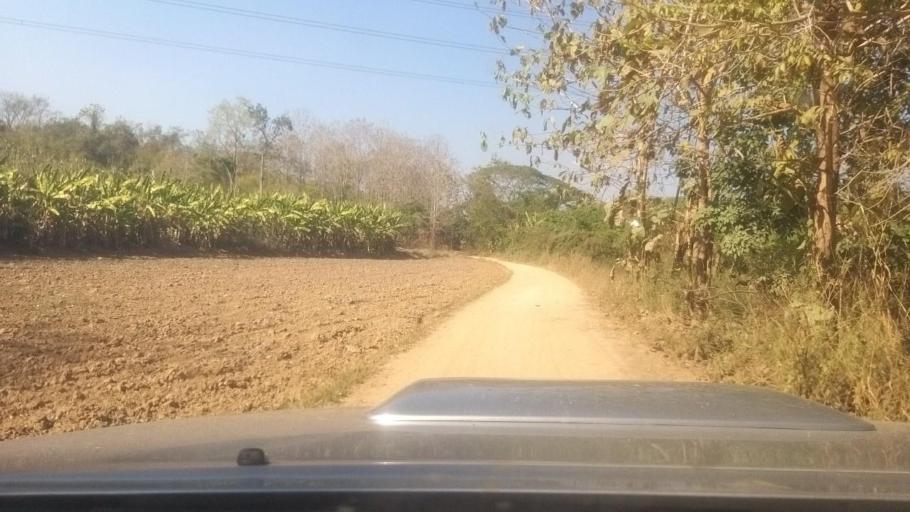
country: TH
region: Phrae
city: Nong Muang Khai
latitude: 18.3093
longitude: 100.0294
